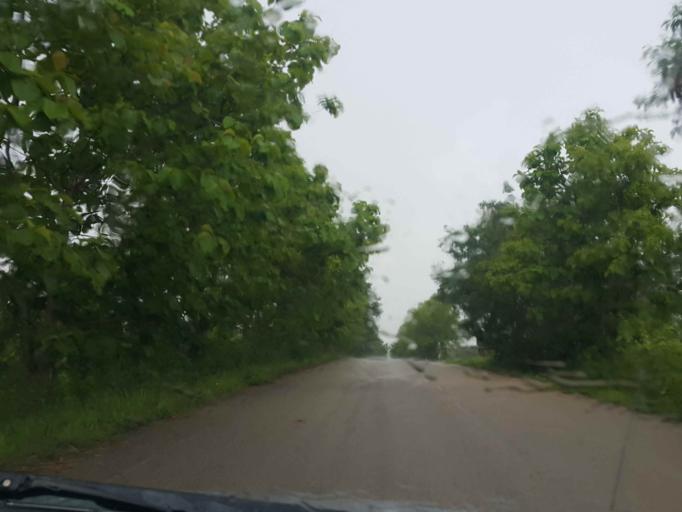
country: TH
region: Phayao
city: Dok Kham Tai
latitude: 19.0103
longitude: 100.0622
